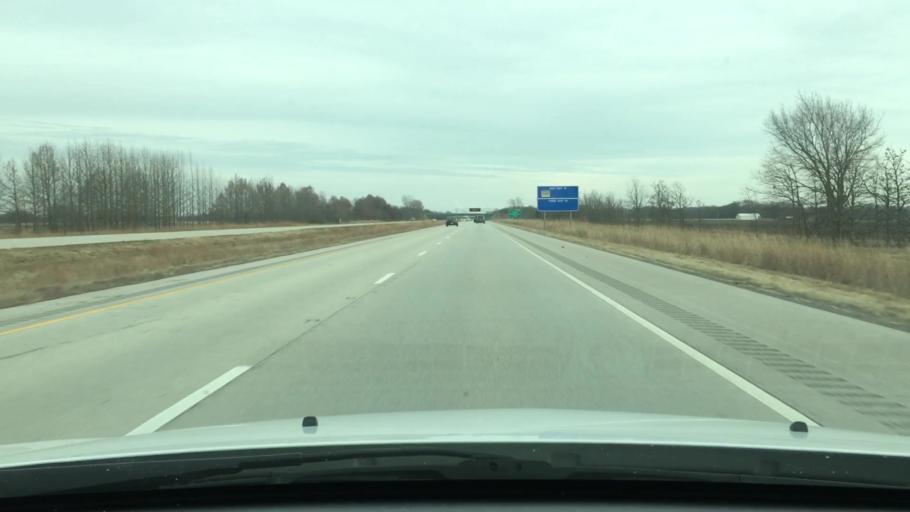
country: US
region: Illinois
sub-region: Sangamon County
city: Jerome
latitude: 39.7517
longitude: -89.7812
